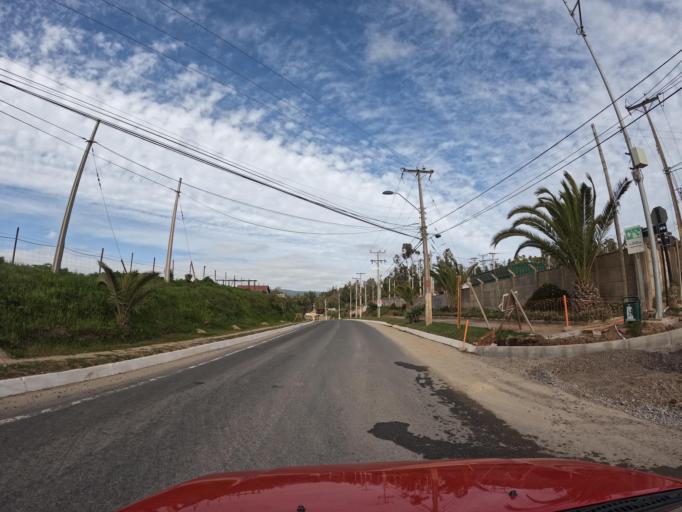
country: CL
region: O'Higgins
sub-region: Provincia de Colchagua
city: Santa Cruz
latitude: -34.3865
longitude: -71.9914
